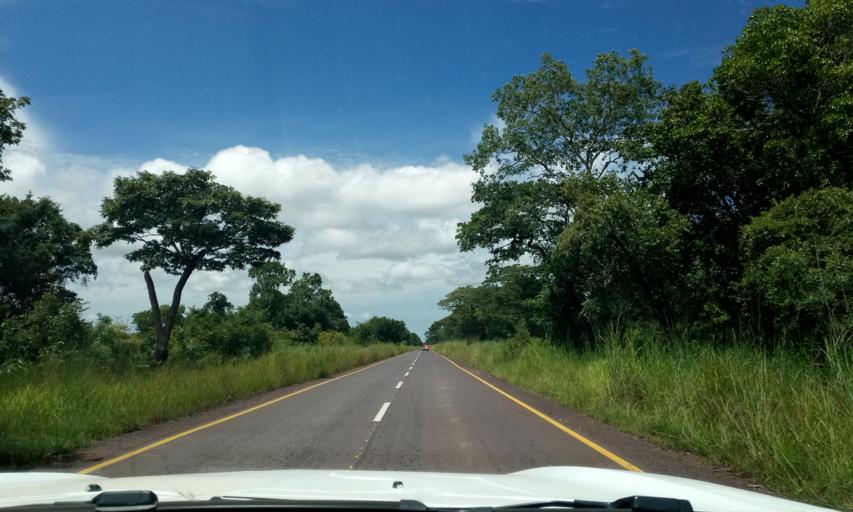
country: CD
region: Katanga
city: Lubumbashi
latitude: -11.1026
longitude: 27.9781
